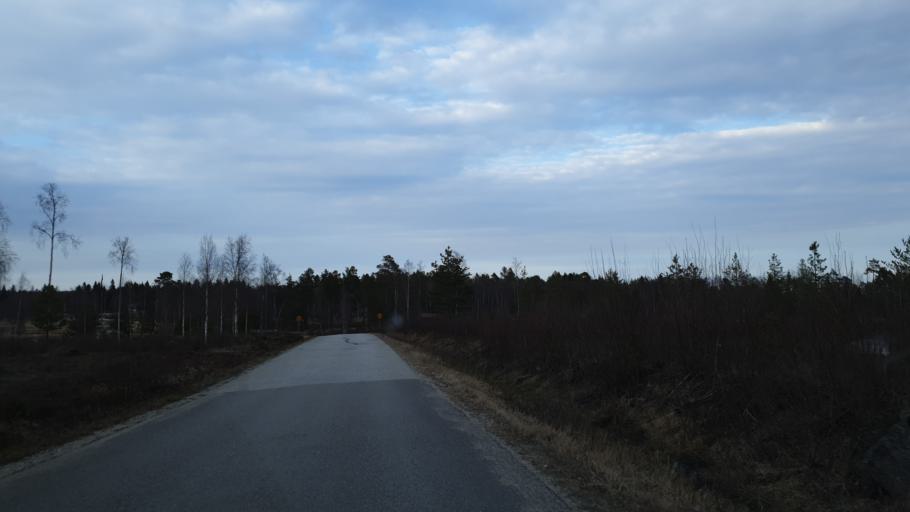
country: SE
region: Vaesternorrland
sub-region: Sundsvalls Kommun
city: Njurundabommen
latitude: 62.0174
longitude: 17.4042
